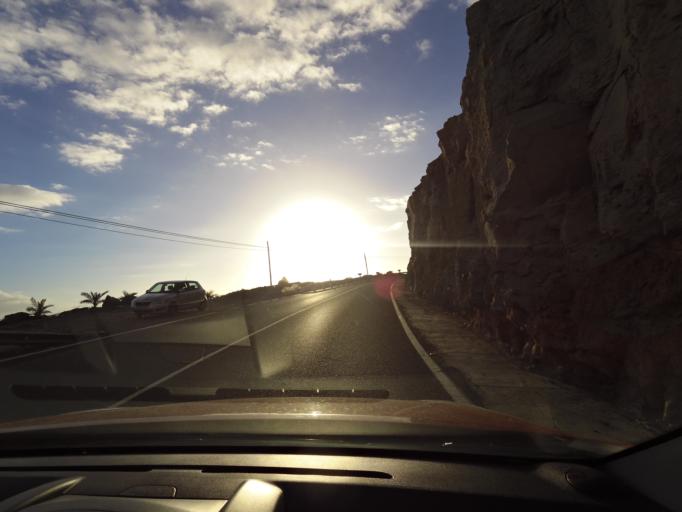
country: ES
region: Canary Islands
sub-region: Provincia de Las Palmas
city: Puerto Rico
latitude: 27.7982
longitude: -15.7343
